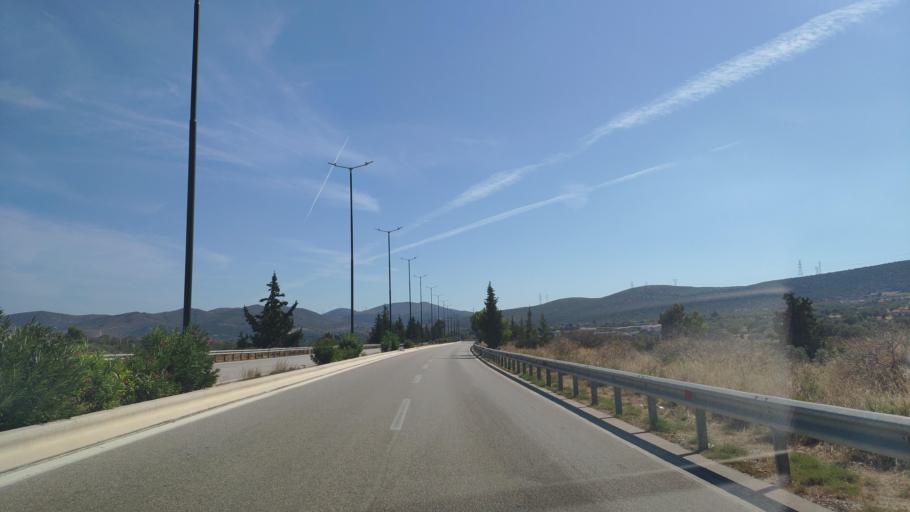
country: GR
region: Attica
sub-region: Nomarchia Anatolikis Attikis
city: Keratea
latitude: 37.8088
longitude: 23.9882
